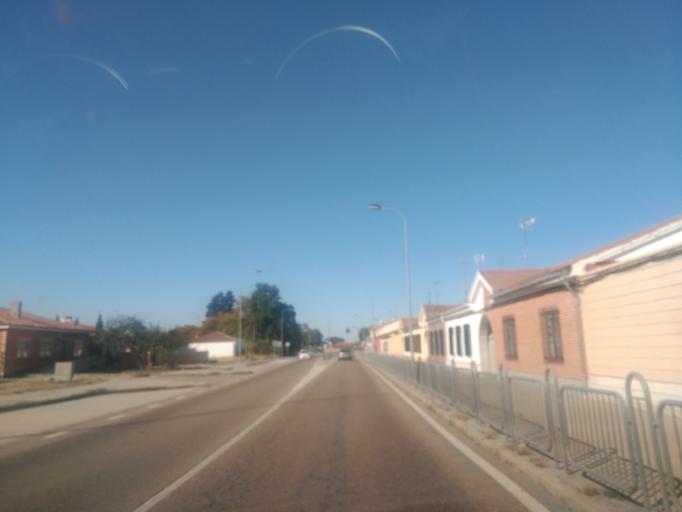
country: ES
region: Castille and Leon
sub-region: Provincia de Valladolid
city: Sardon de Duero
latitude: 41.6076
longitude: -4.4315
